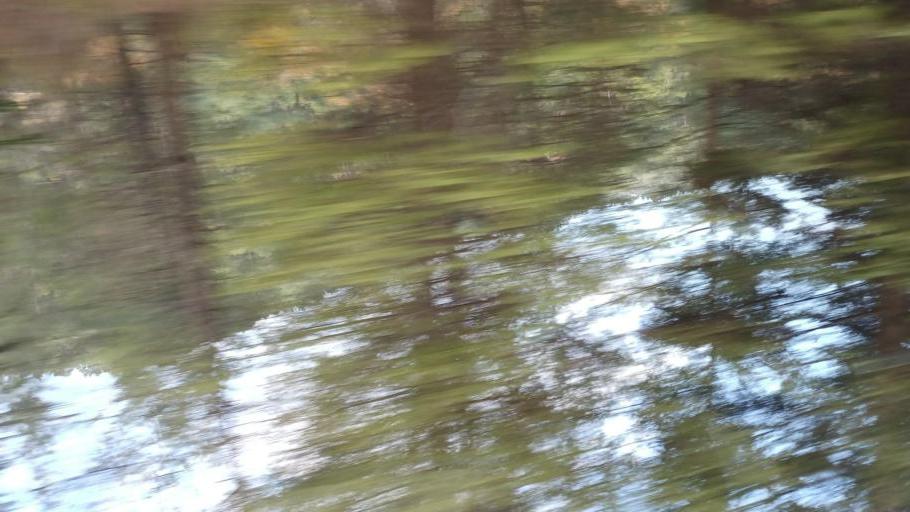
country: CY
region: Limassol
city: Kyperounta
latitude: 34.9275
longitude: 32.9346
